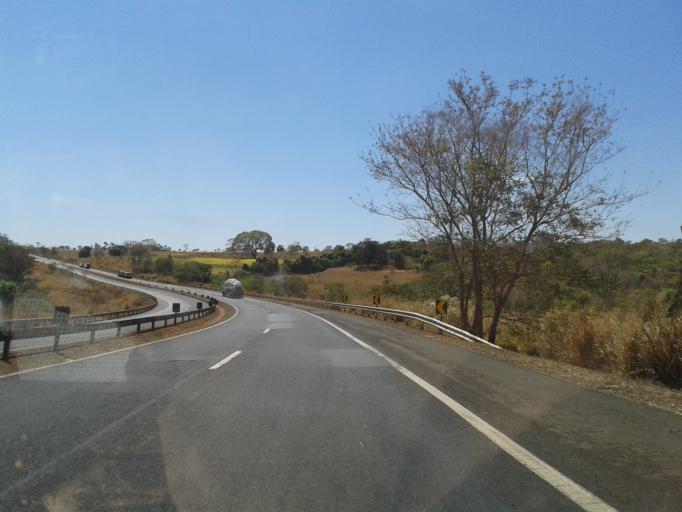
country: BR
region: Minas Gerais
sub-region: Monte Alegre De Minas
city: Monte Alegre de Minas
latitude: -18.8325
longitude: -49.0895
